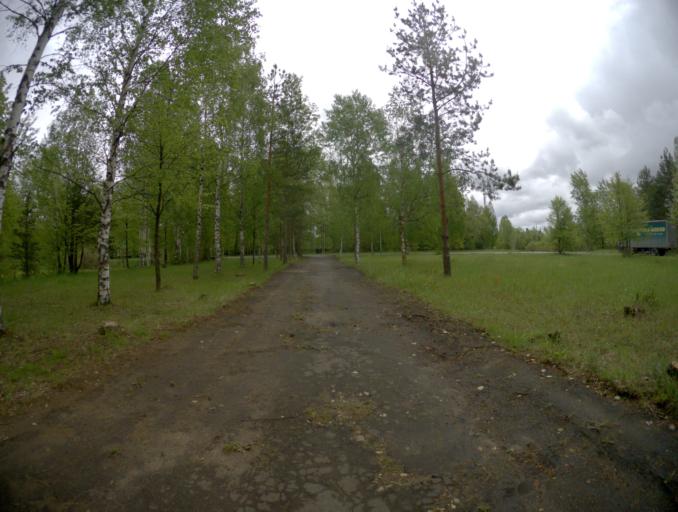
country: RU
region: Rjazan
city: Gus'-Zheleznyy
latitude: 55.2446
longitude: 41.0451
